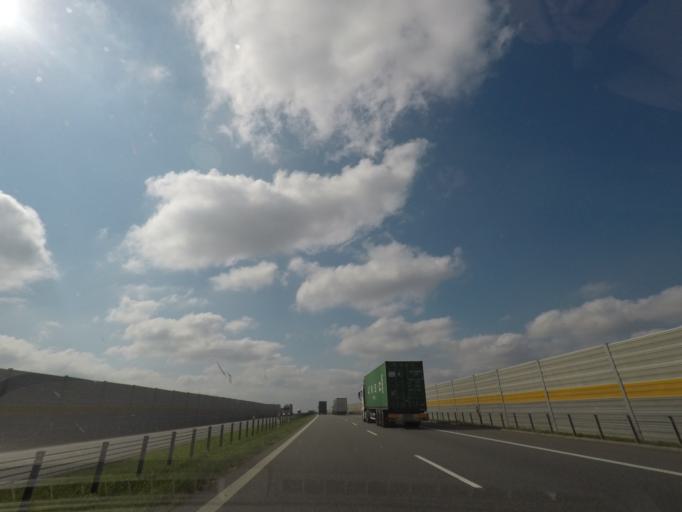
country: PL
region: Kujawsko-Pomorskie
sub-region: Powiat torunski
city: Lubicz Dolny
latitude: 53.1317
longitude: 18.7395
